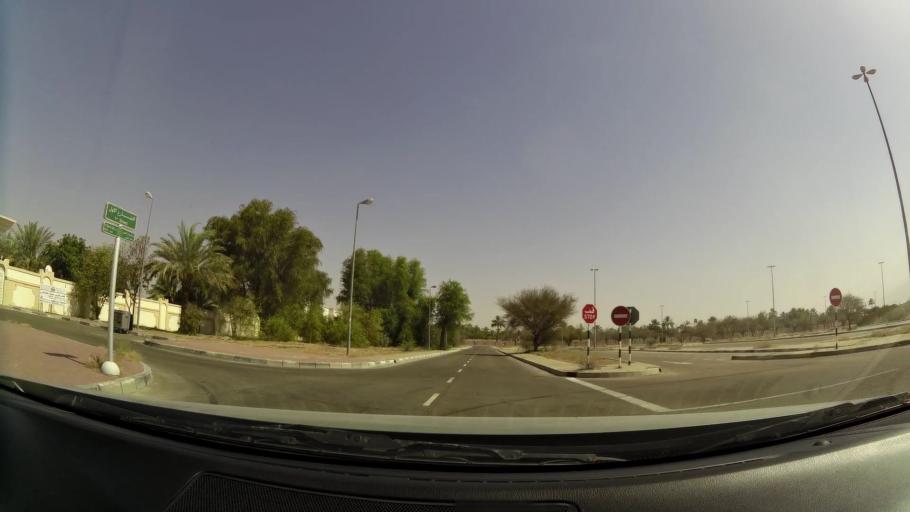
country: OM
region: Al Buraimi
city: Al Buraymi
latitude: 24.2992
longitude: 55.7805
